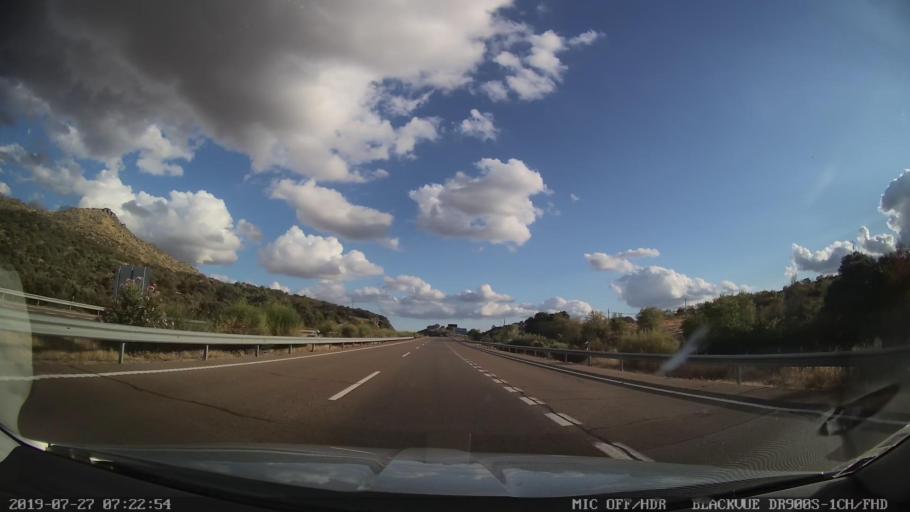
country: ES
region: Extremadura
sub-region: Provincia de Caceres
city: Santa Cruz de la Sierra
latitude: 39.3318
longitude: -5.8572
